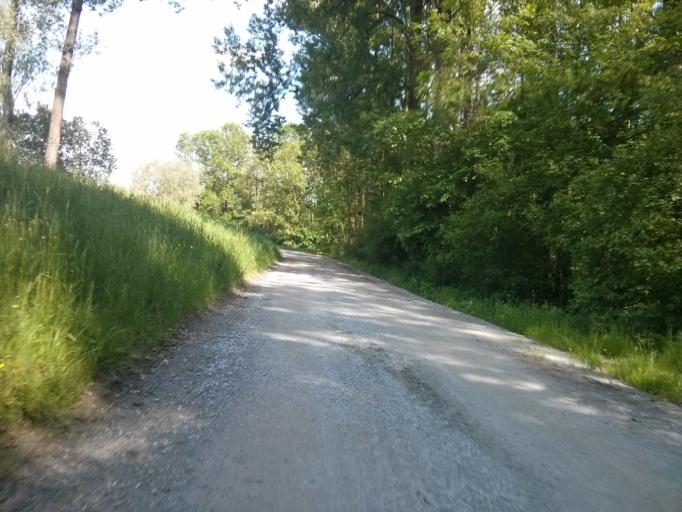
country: DE
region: Bavaria
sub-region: Lower Bavaria
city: Plattling
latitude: 48.7778
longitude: 12.9095
